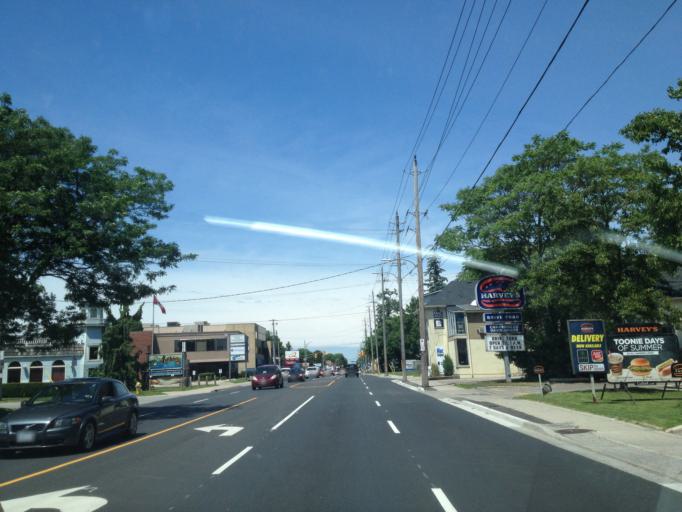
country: CA
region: Ontario
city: London
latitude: 42.9718
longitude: -81.2619
